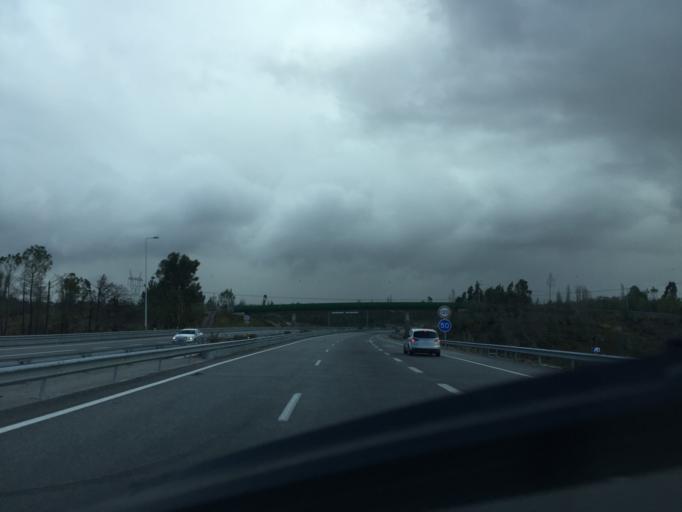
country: PT
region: Coimbra
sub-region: Cantanhede
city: Cantanhede
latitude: 40.2854
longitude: -8.5223
